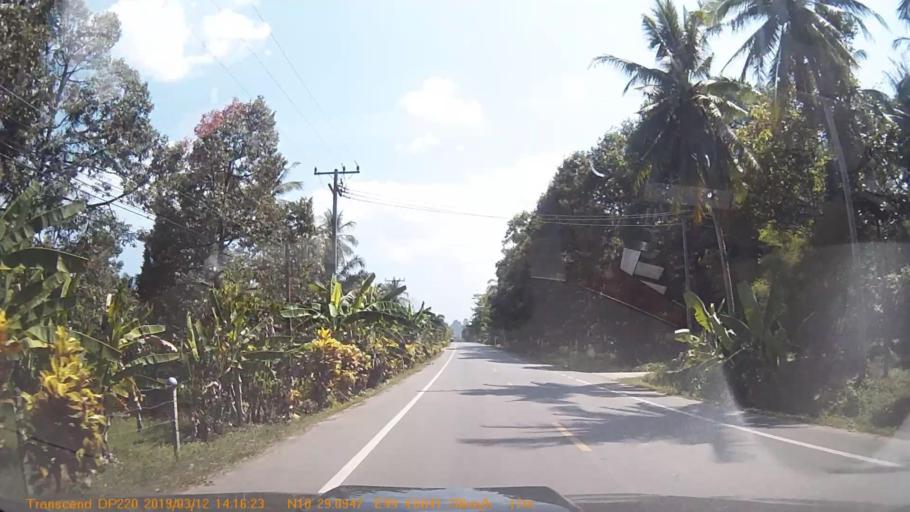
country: TH
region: Chumphon
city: Chumphon
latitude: 10.4845
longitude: 99.0768
